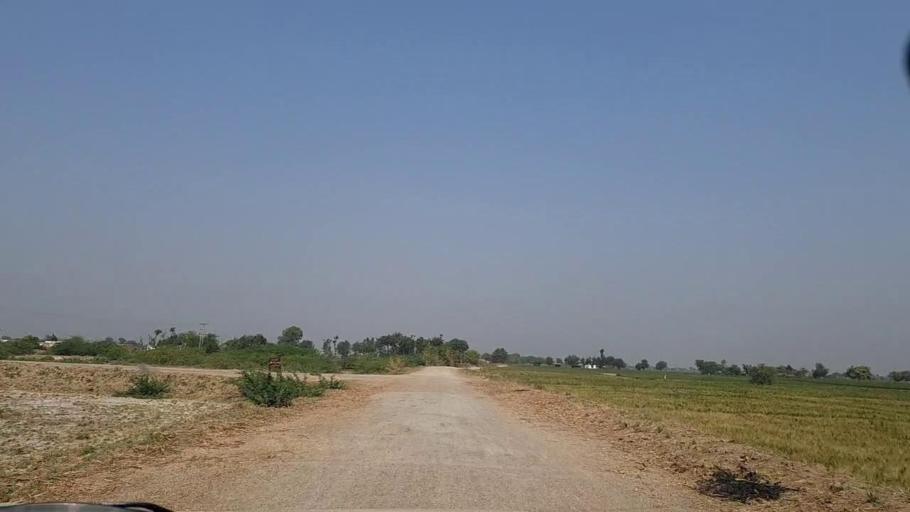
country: PK
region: Sindh
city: Mirpur Khas
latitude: 25.4978
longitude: 69.1909
